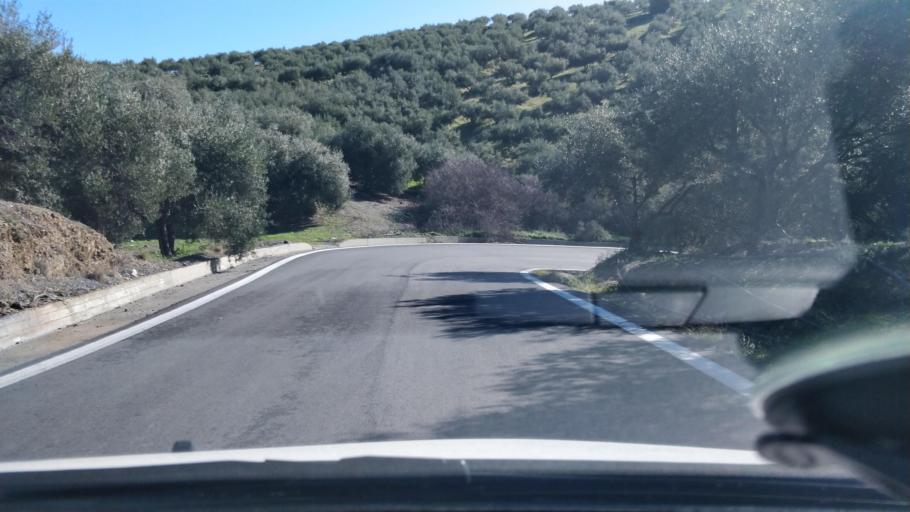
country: GR
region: Crete
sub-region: Nomos Irakleiou
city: Arkalochori
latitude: 35.0060
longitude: 25.4407
